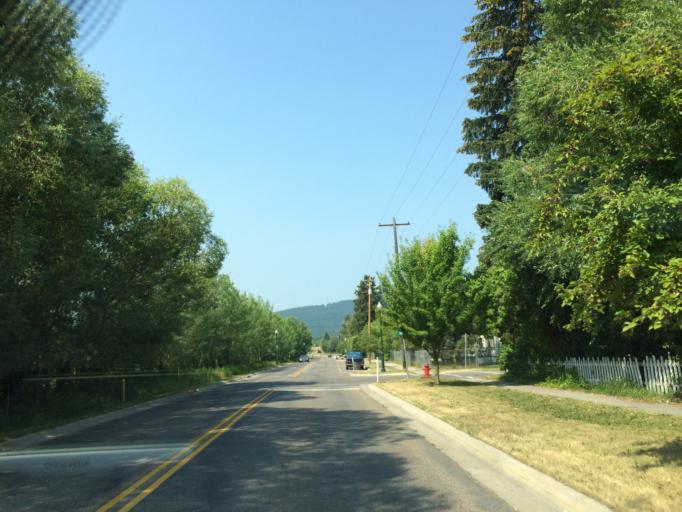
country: US
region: Montana
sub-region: Flathead County
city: Whitefish
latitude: 48.4152
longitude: -114.3431
